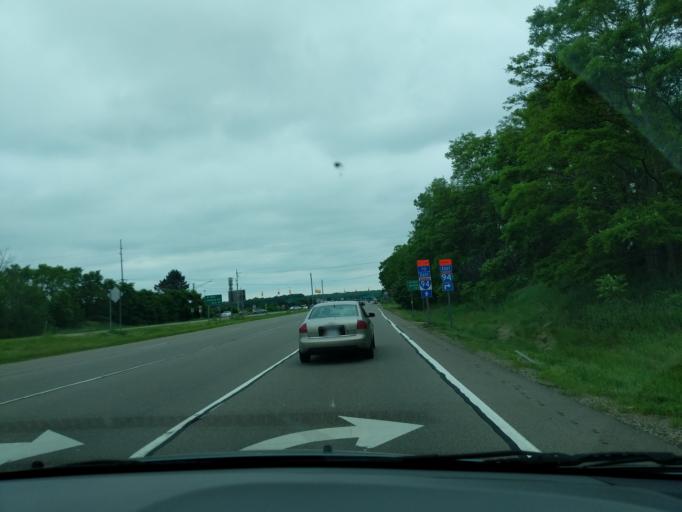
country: US
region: Michigan
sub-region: Calhoun County
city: Lakeview
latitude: 42.2594
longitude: -85.1813
